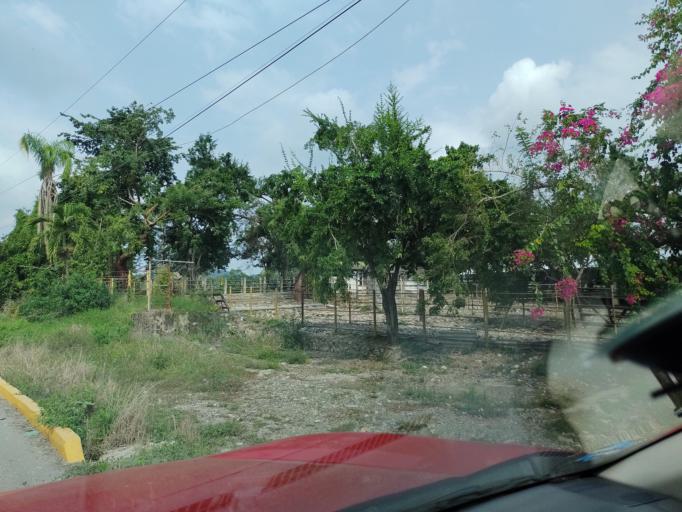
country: MX
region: Veracruz
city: Agua Dulce
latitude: 20.3743
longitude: -97.2982
